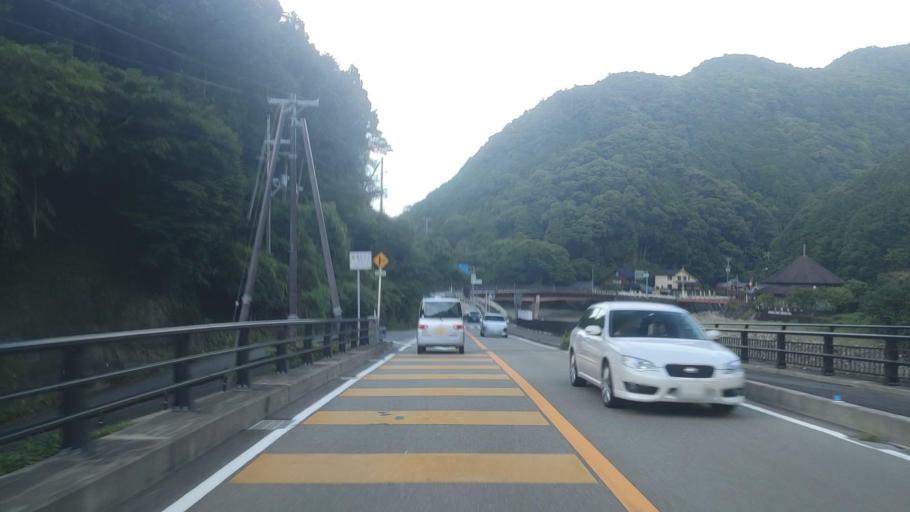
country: JP
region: Wakayama
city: Tanabe
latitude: 33.7743
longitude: 135.5026
